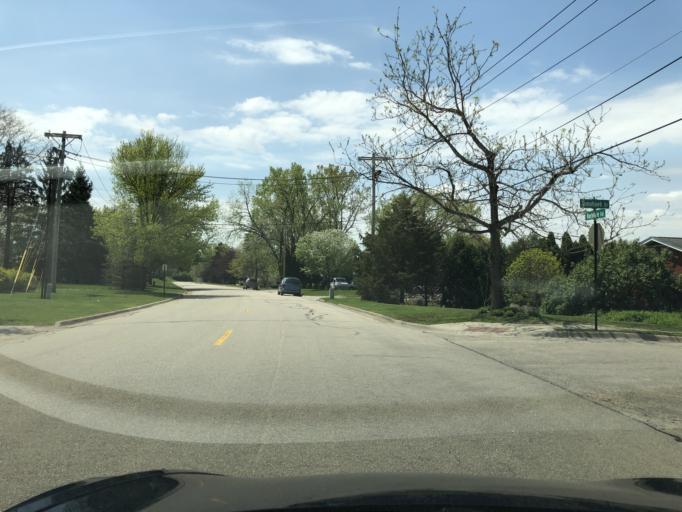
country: US
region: Iowa
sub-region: Dubuque County
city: Dubuque
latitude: 42.4749
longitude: -90.6700
